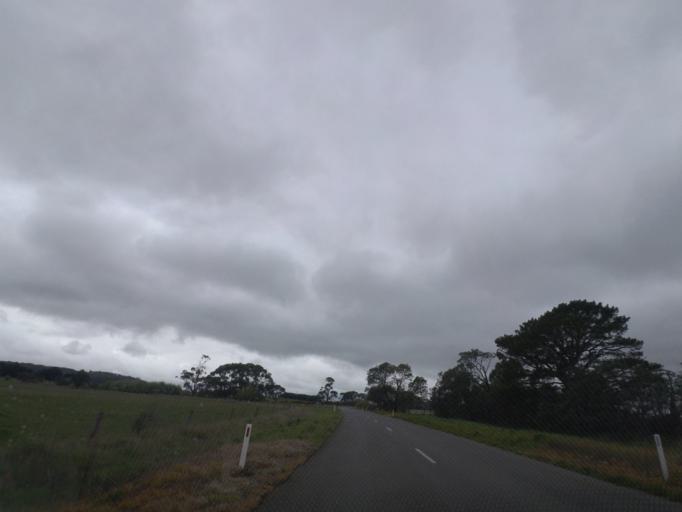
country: AU
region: Victoria
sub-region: Hume
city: Sunbury
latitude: -37.3248
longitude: 144.5590
